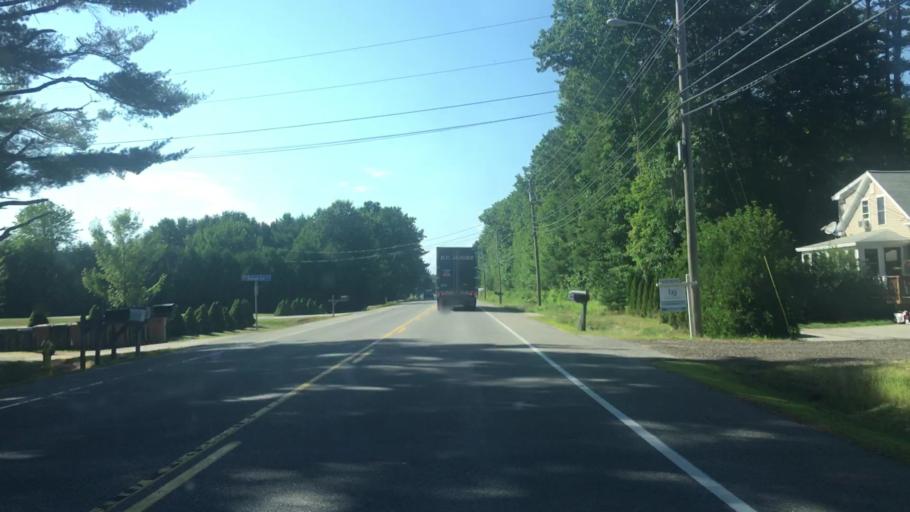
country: US
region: Maine
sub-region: York County
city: Saco
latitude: 43.5393
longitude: -70.4795
